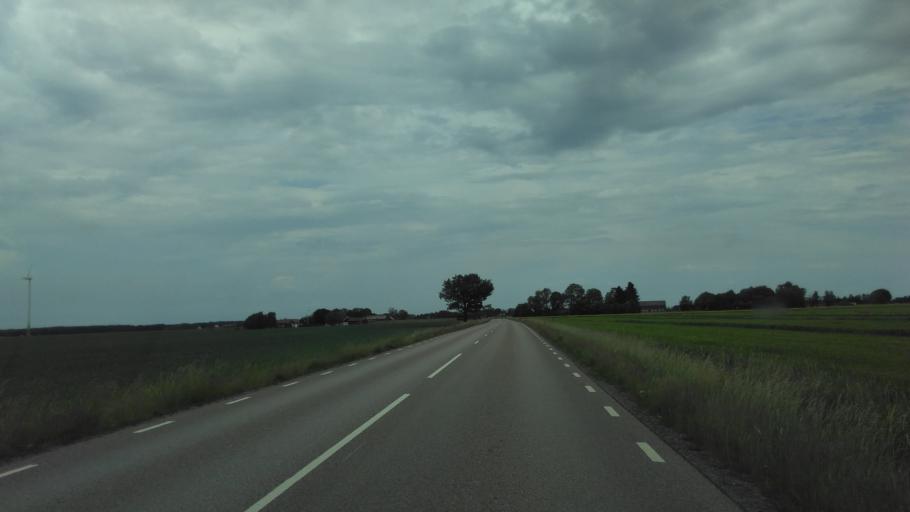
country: SE
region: Vaestra Goetaland
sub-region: Lidkopings Kommun
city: Lidkoping
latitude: 58.4029
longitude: 13.1622
